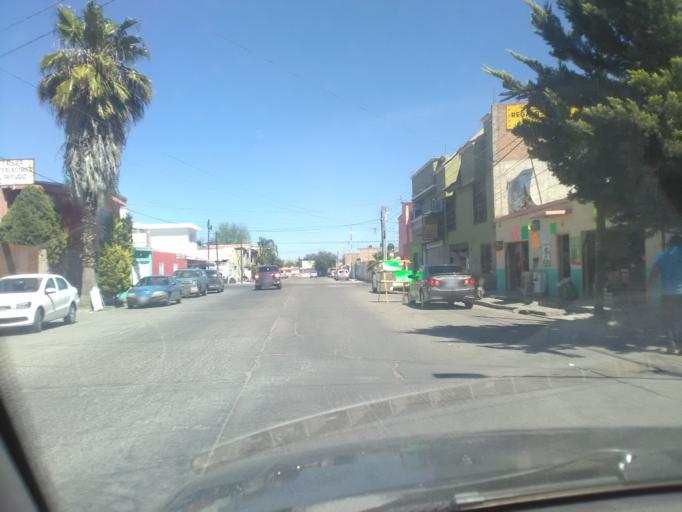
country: MX
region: Durango
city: Victoria de Durango
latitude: 24.0156
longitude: -104.6578
